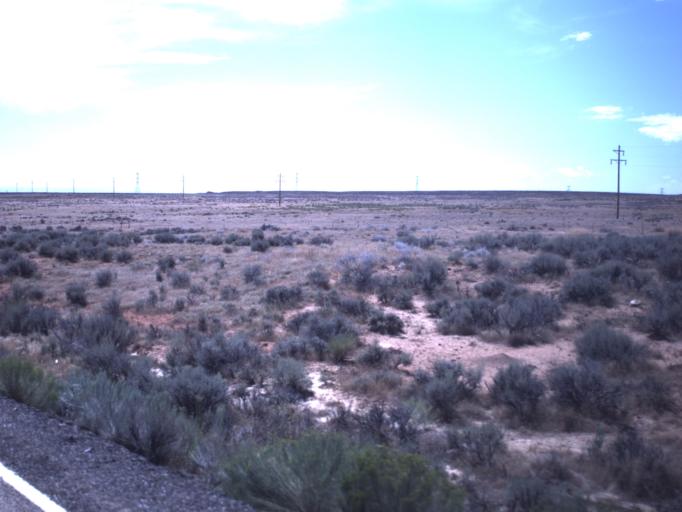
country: US
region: Utah
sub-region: Uintah County
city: Maeser
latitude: 40.2890
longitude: -109.6848
